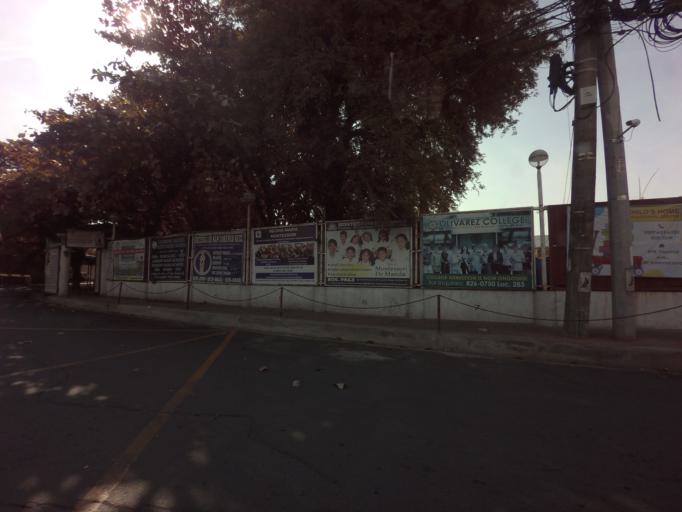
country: PH
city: Sambayanihan People's Village
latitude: 14.4675
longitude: 121.0102
